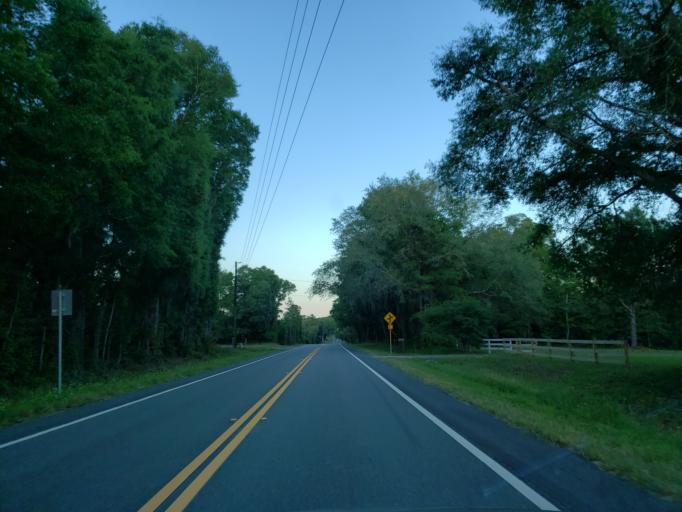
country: US
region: Georgia
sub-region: Echols County
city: Statenville
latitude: 30.5813
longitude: -83.2084
